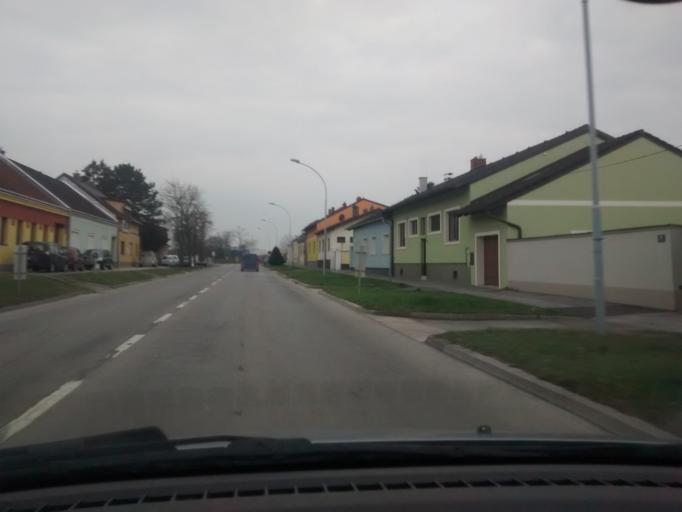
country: AT
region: Lower Austria
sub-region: Politischer Bezirk Wien-Umgebung
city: Fischamend Dorf
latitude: 48.1172
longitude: 16.6055
